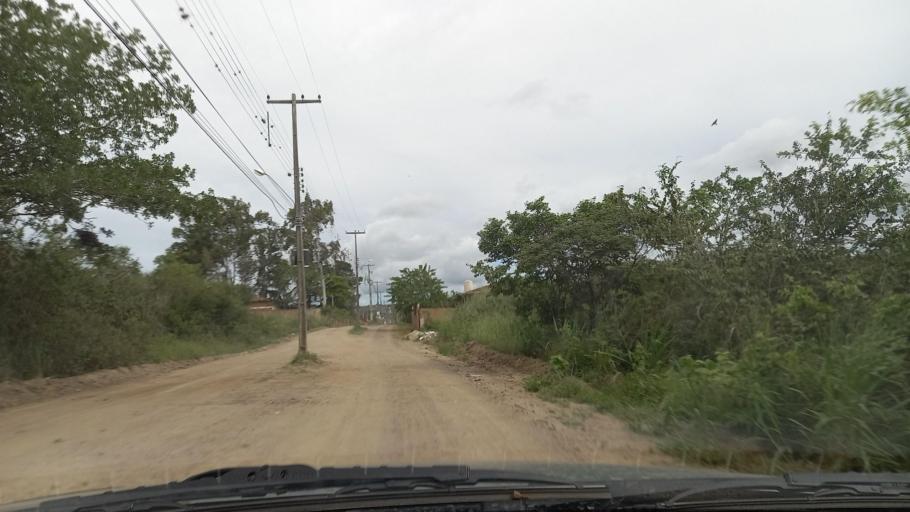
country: BR
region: Pernambuco
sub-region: Gravata
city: Gravata
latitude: -8.1975
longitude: -35.6004
